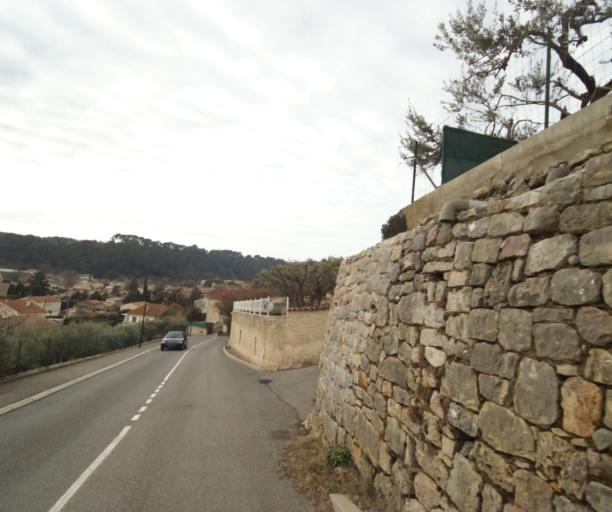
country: FR
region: Provence-Alpes-Cote d'Azur
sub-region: Departement du Var
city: Trans-en-Provence
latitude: 43.5072
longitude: 6.4885
